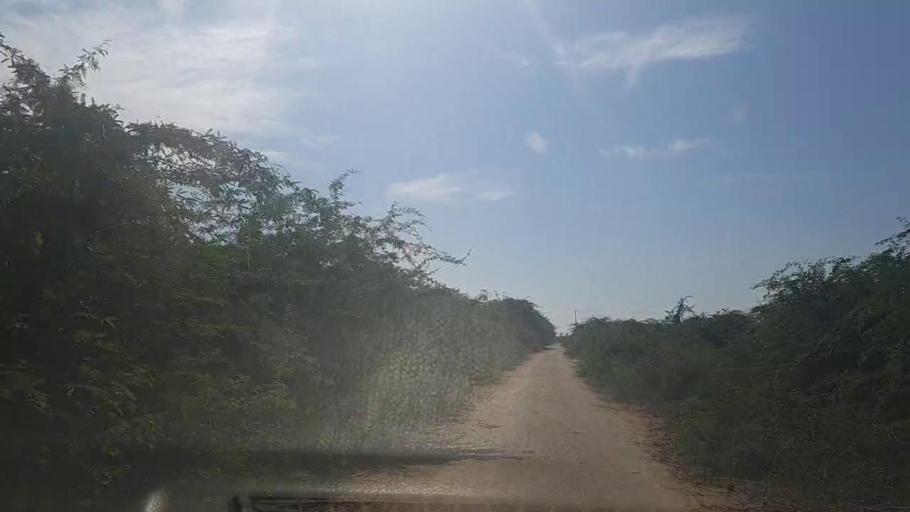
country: PK
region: Sindh
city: Mirpur Batoro
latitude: 24.6744
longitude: 68.1829
